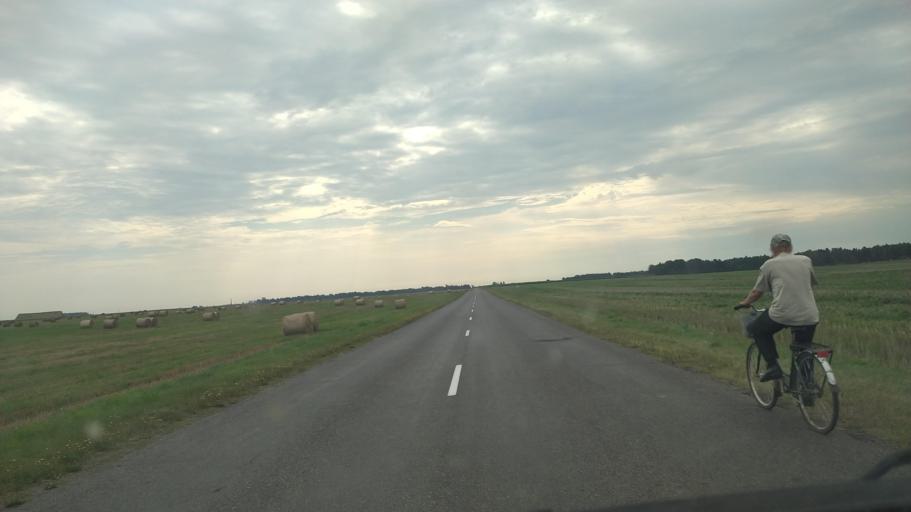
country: BY
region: Brest
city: Byaroza
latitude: 52.5749
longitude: 24.8767
